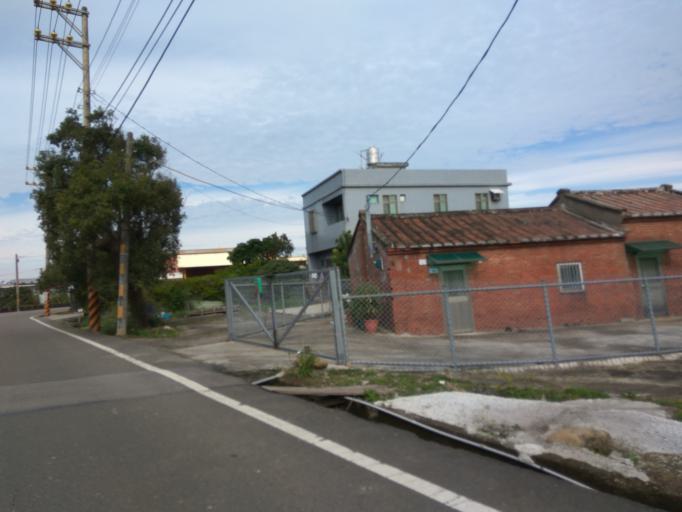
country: TW
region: Taiwan
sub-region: Hsinchu
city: Zhubei
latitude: 24.9556
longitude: 121.1113
